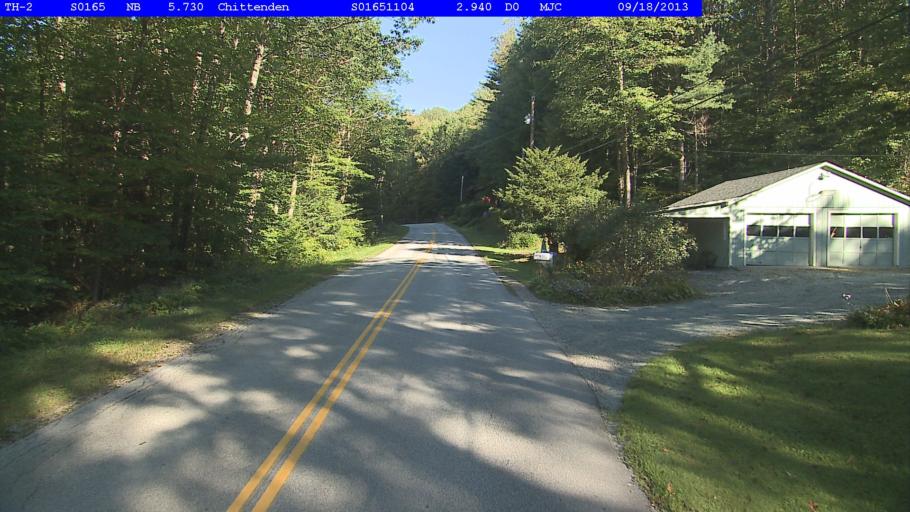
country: US
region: Vermont
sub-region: Rutland County
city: Rutland
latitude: 43.7179
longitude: -72.9629
